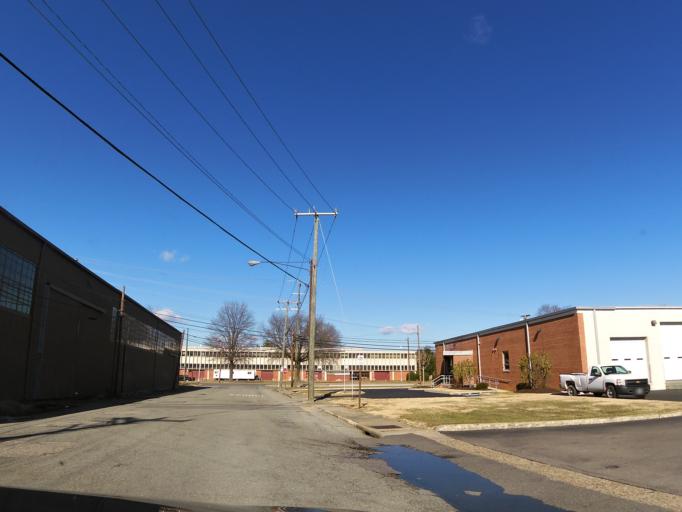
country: US
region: Virginia
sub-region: City of Richmond
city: Richmond
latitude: 37.5775
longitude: -77.4698
